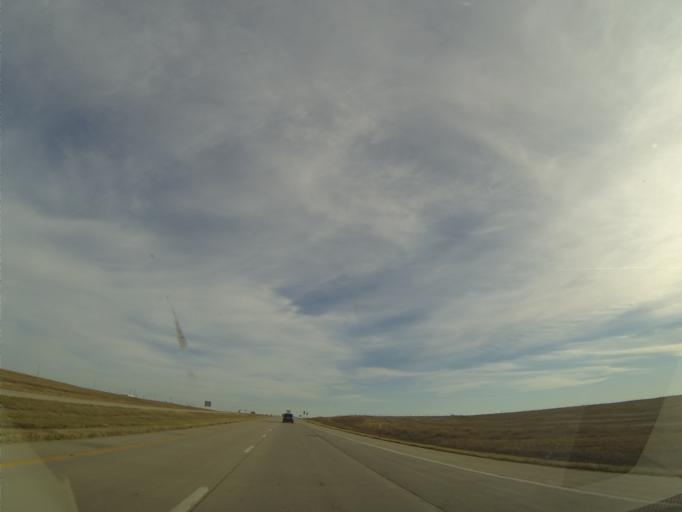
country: US
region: Kansas
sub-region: Ottawa County
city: Minneapolis
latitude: 39.1120
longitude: -97.6614
